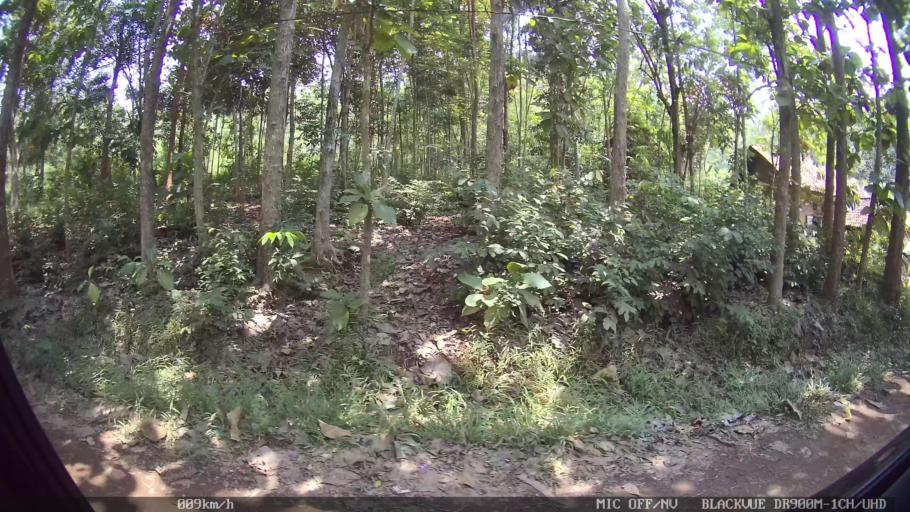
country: ID
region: Lampung
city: Pringsewu
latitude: -5.3806
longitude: 105.0035
